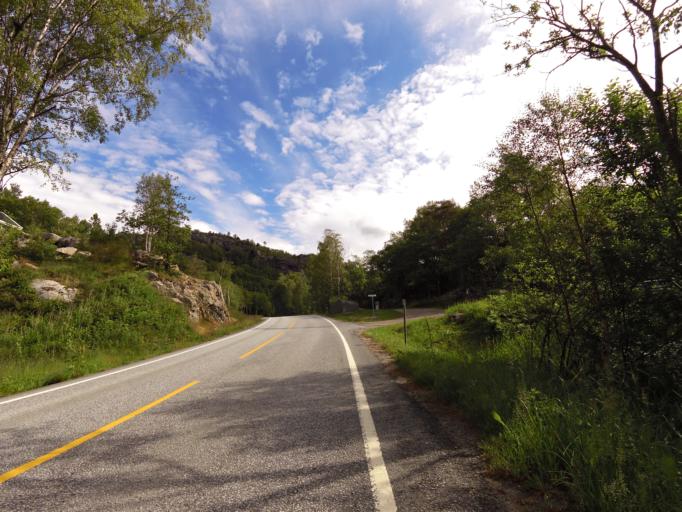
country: NO
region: Vest-Agder
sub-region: Lyngdal
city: Lyngdal
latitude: 58.0473
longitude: 7.1677
